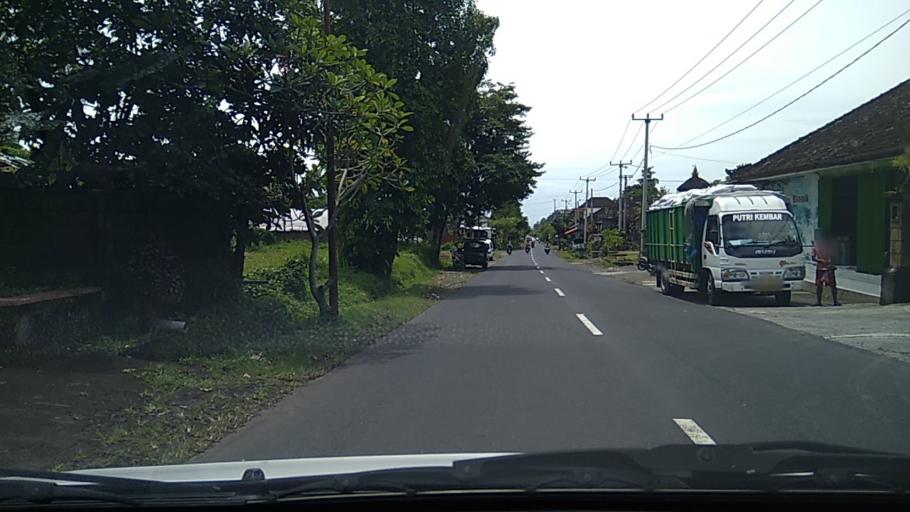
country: ID
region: Bali
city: Wanasari Baleran
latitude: -8.4713
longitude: 115.1370
